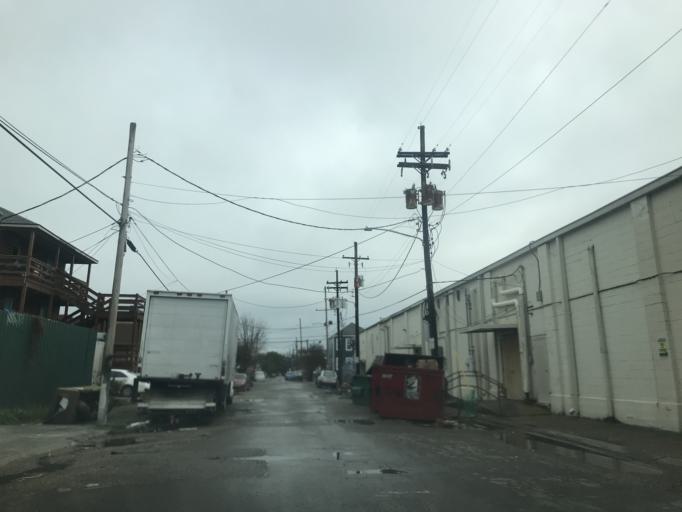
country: US
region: Louisiana
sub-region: Orleans Parish
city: New Orleans
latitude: 29.9698
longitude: -90.1073
